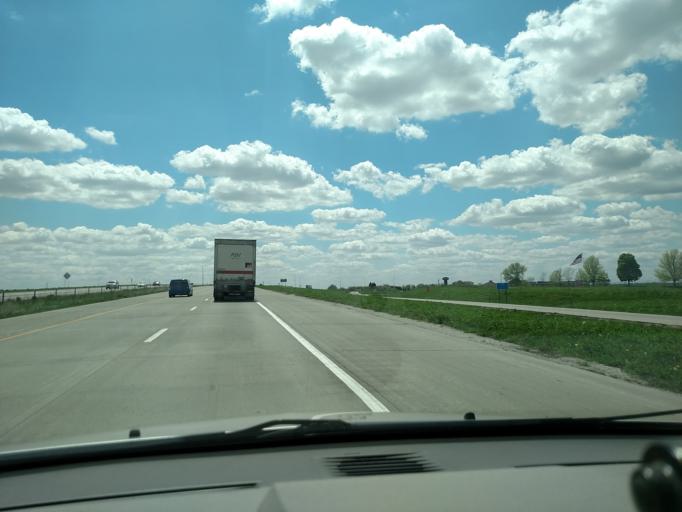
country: US
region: Iowa
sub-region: Polk County
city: Ankeny
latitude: 41.7648
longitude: -93.5698
